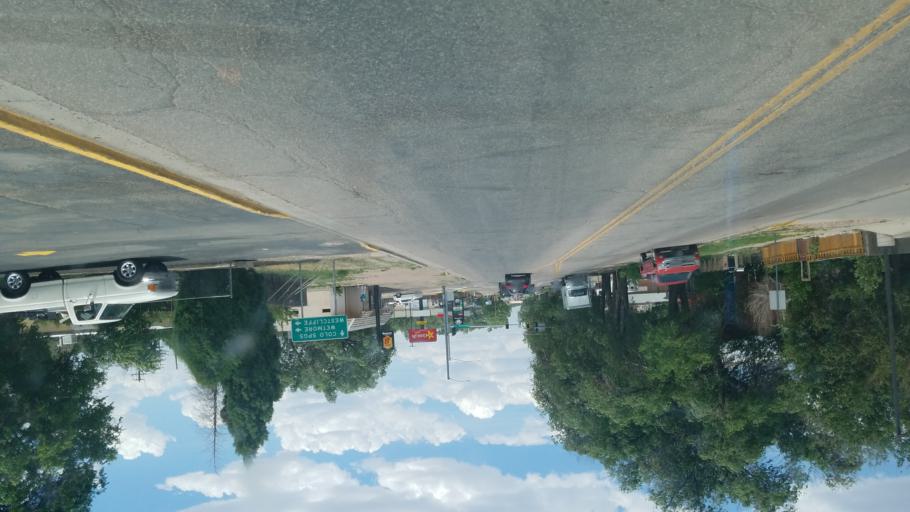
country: US
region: Colorado
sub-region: Fremont County
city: Florence
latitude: 38.3891
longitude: -105.1132
